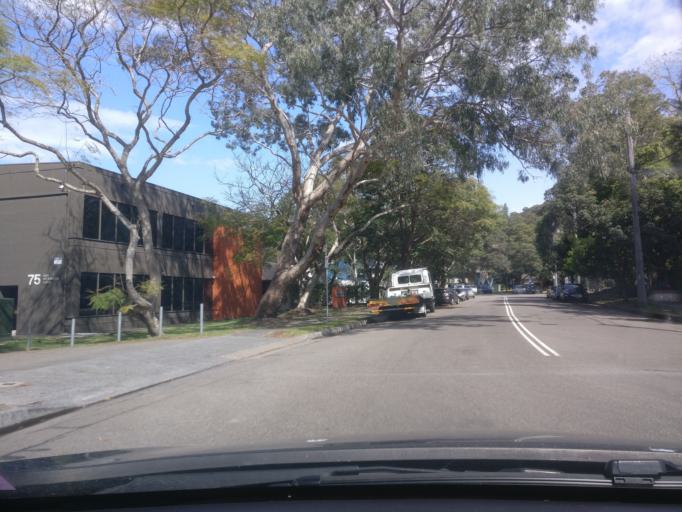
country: AU
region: New South Wales
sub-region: Warringah
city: Brookvale
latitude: -33.7639
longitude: 151.2636
